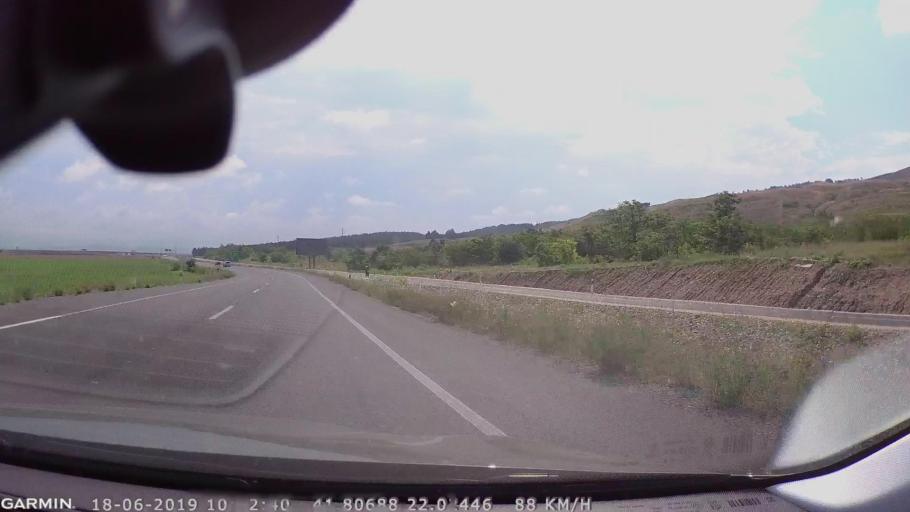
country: MK
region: Sveti Nikole
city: Sveti Nikole
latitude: 41.8205
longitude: 22.0140
